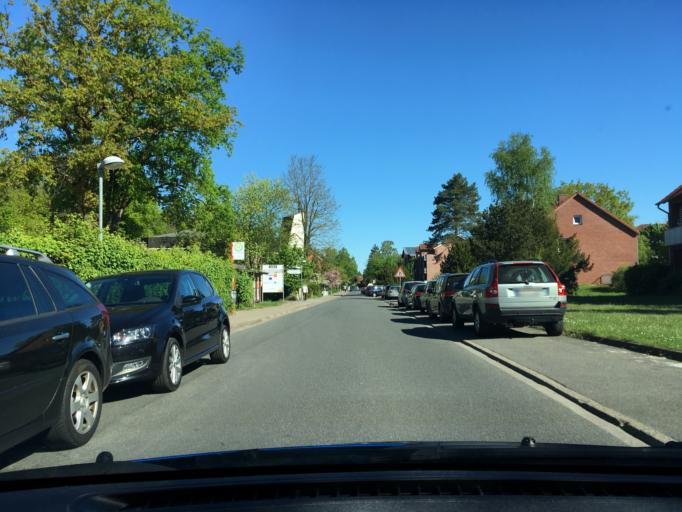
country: DE
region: Lower Saxony
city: Lueneburg
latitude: 53.2250
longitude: 10.3987
